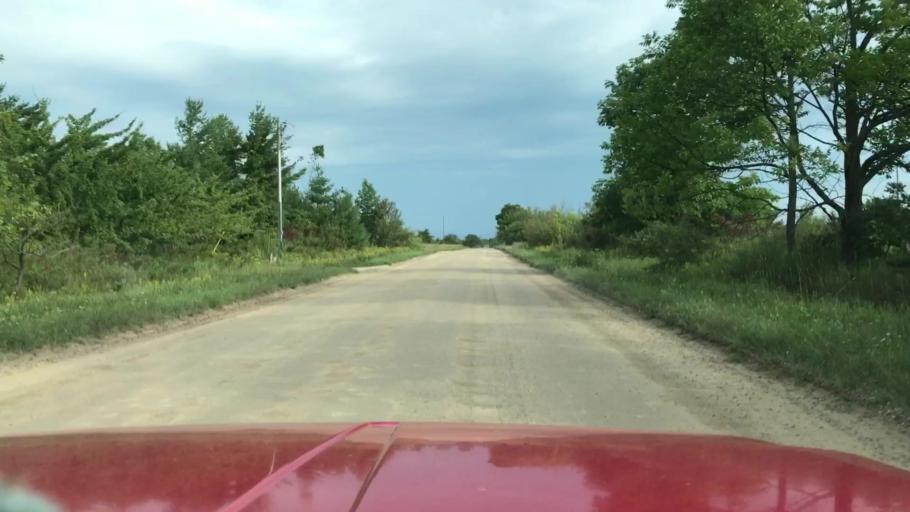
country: US
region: Michigan
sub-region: Charlevoix County
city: Charlevoix
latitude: 45.7236
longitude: -85.5158
